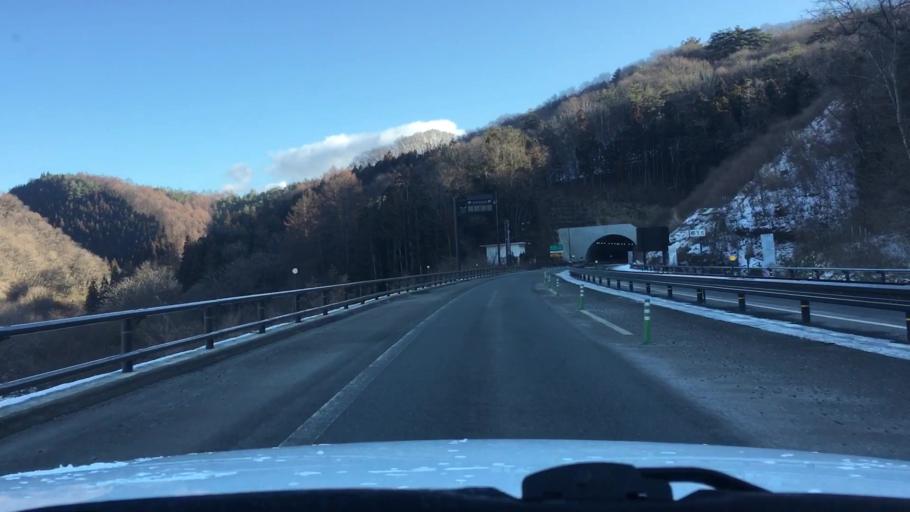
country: JP
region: Iwate
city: Morioka-shi
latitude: 39.6733
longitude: 141.2175
